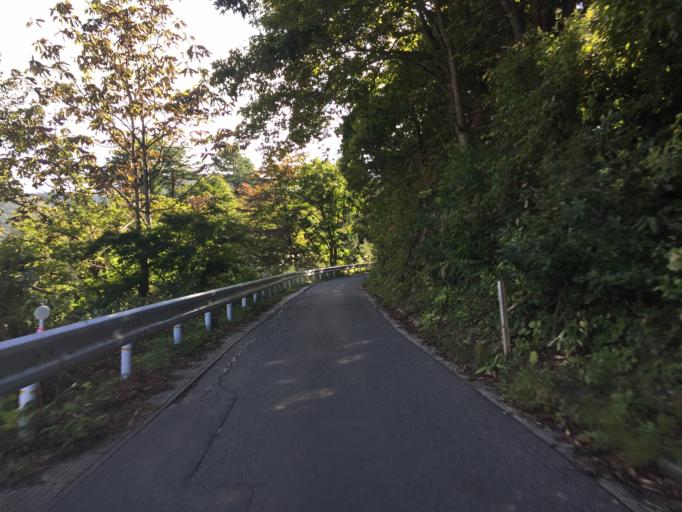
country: JP
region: Yamagata
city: Yonezawa
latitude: 37.8103
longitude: 140.2616
